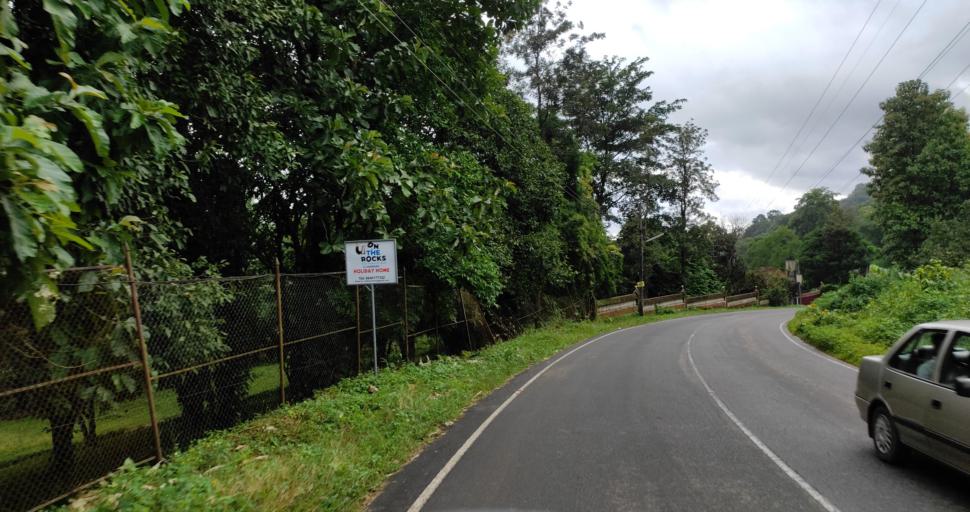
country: IN
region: Kerala
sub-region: Ernakulam
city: Angamali
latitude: 10.2905
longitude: 76.5490
